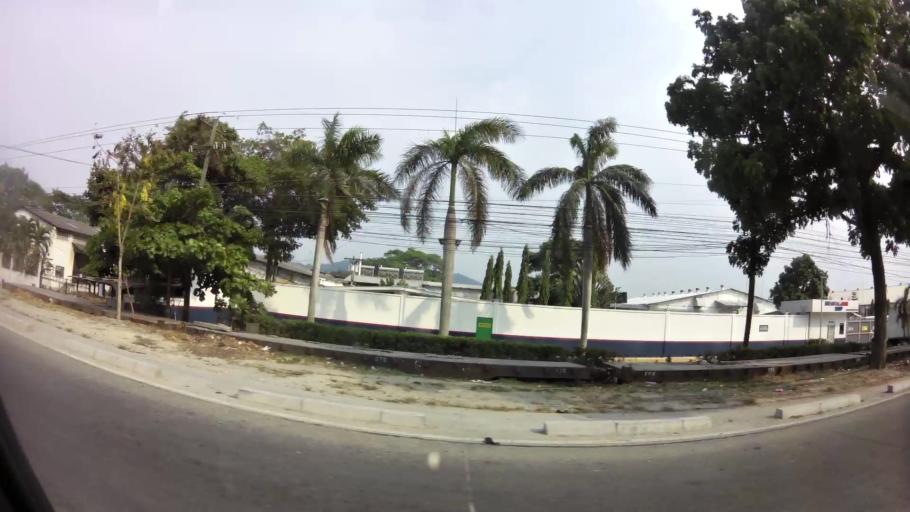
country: HN
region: Cortes
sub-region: San Pedro Sula
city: Pena Blanca
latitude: 15.5528
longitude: -87.9992
